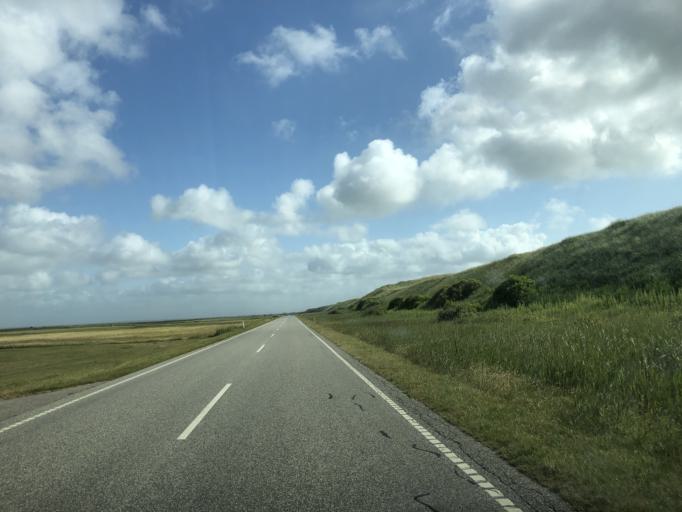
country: DK
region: Central Jutland
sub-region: Lemvig Kommune
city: Harboore
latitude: 56.4115
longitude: 8.1225
